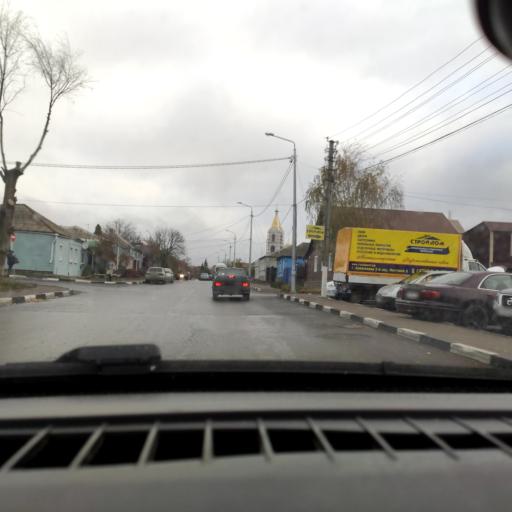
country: RU
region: Belgorod
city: Alekseyevka
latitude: 50.6280
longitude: 38.6915
